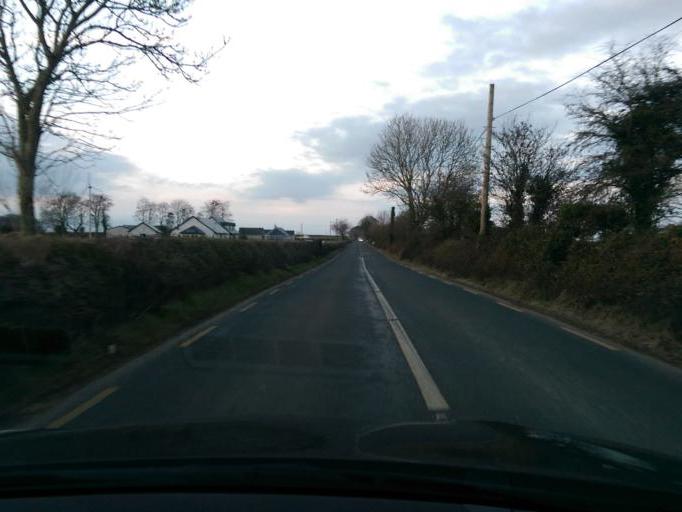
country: IE
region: Connaught
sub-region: County Galway
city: Portumna
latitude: 53.0218
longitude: -8.1250
